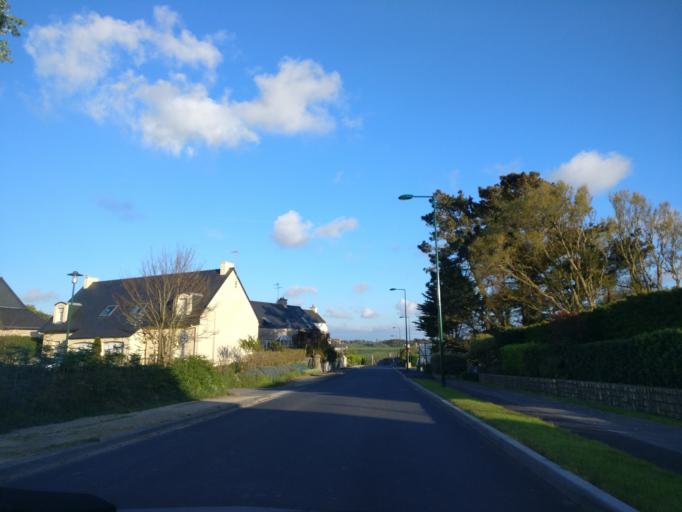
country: FR
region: Brittany
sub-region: Departement du Finistere
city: Porspoder
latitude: 48.4748
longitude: -4.7570
